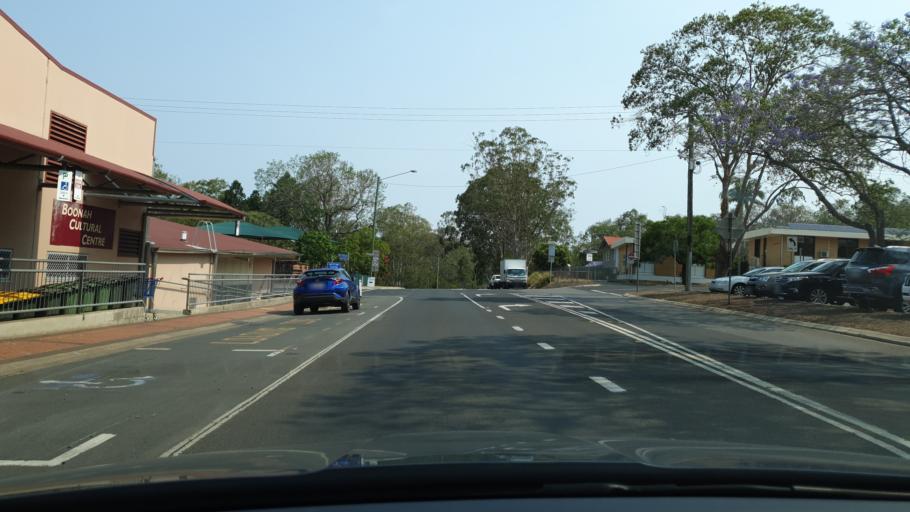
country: AU
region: Queensland
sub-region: Ipswich
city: Deebing Heights
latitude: -27.9983
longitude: 152.6815
